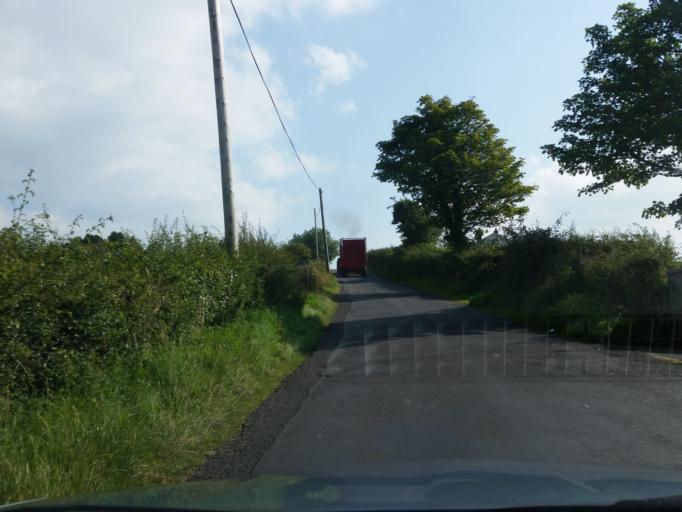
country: GB
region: Northern Ireland
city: Ballinamallard
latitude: 54.3396
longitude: -7.5385
